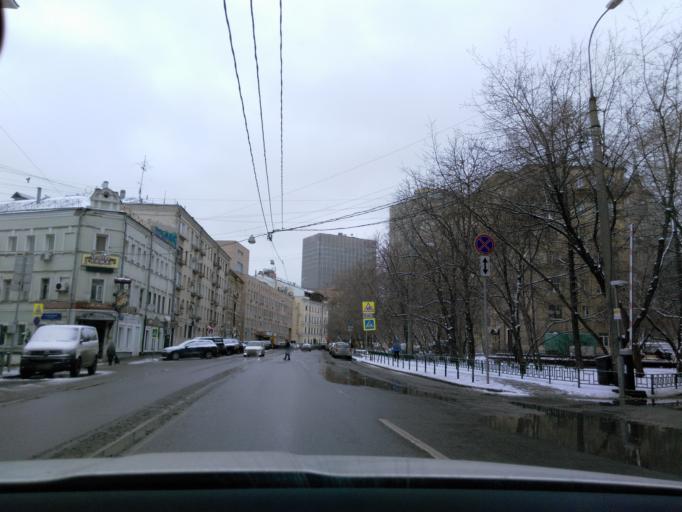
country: RU
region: Moskovskaya
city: Dorogomilovo
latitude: 55.7431
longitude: 37.5782
